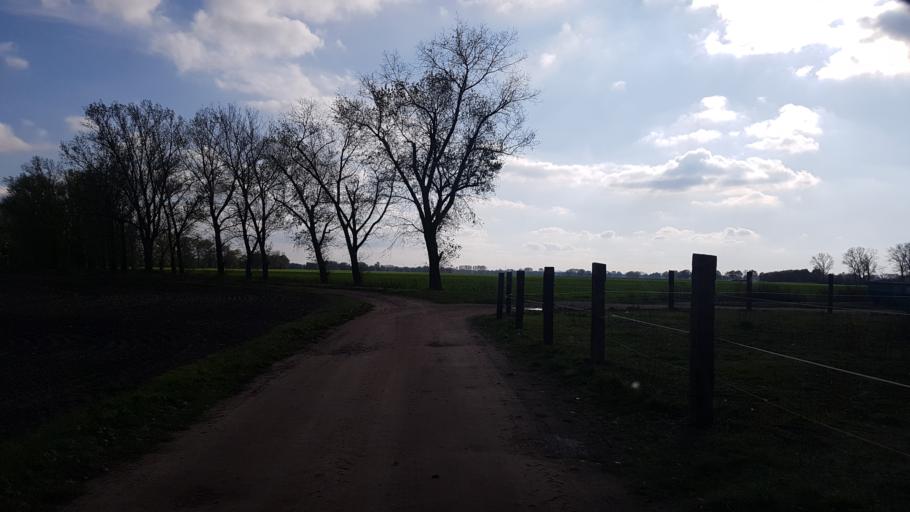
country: DE
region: Brandenburg
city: Schonewalde
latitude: 51.6923
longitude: 13.5722
